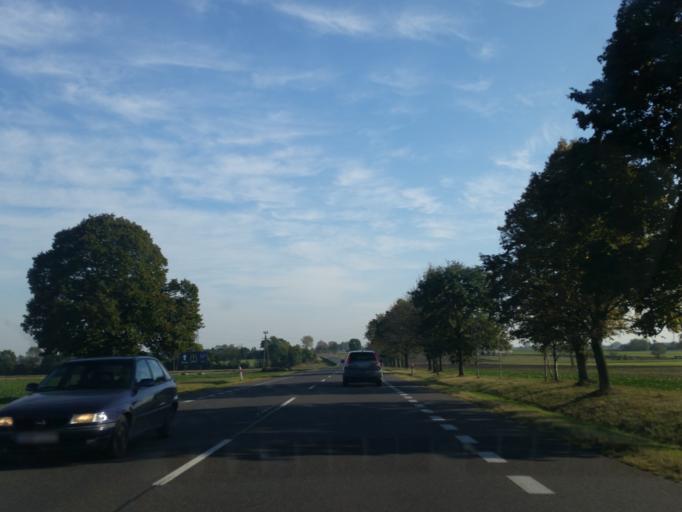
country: PL
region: Masovian Voivodeship
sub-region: Powiat plocki
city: Drobin
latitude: 52.7290
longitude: 20.0056
